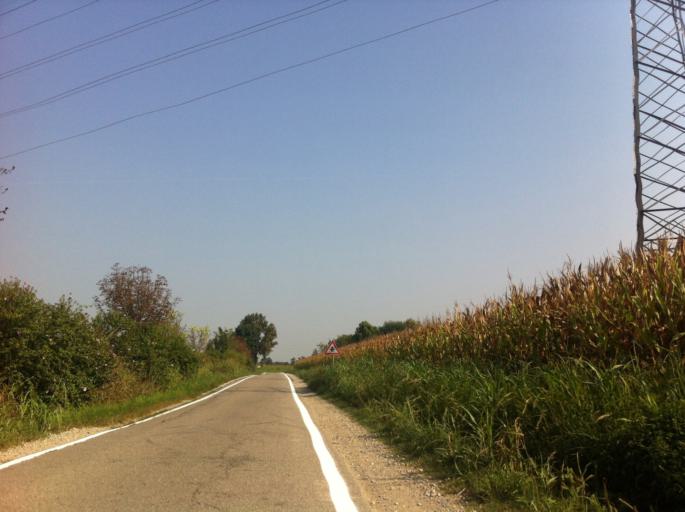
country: IT
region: Lombardy
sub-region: Provincia di Lodi
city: Quartiano
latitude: 45.3455
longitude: 9.4119
